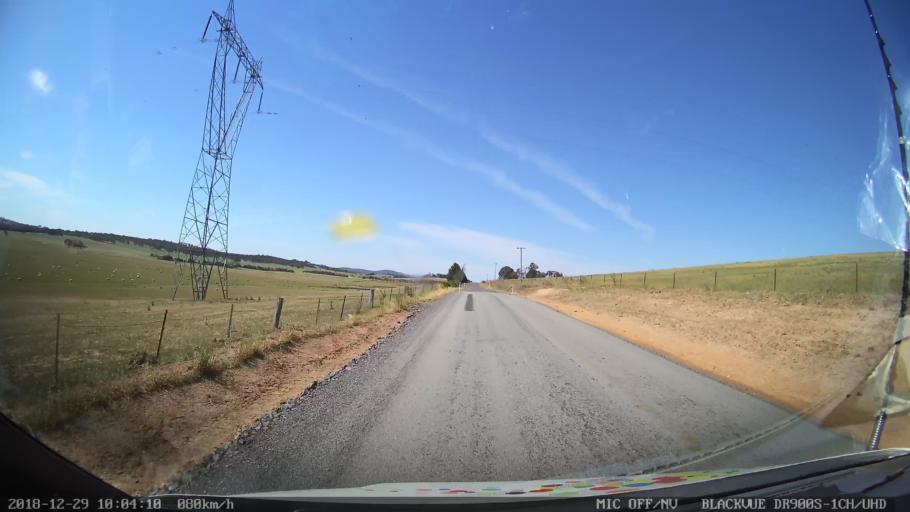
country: AU
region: New South Wales
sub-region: Goulburn Mulwaree
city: Goulburn
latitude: -34.8190
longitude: 149.4560
